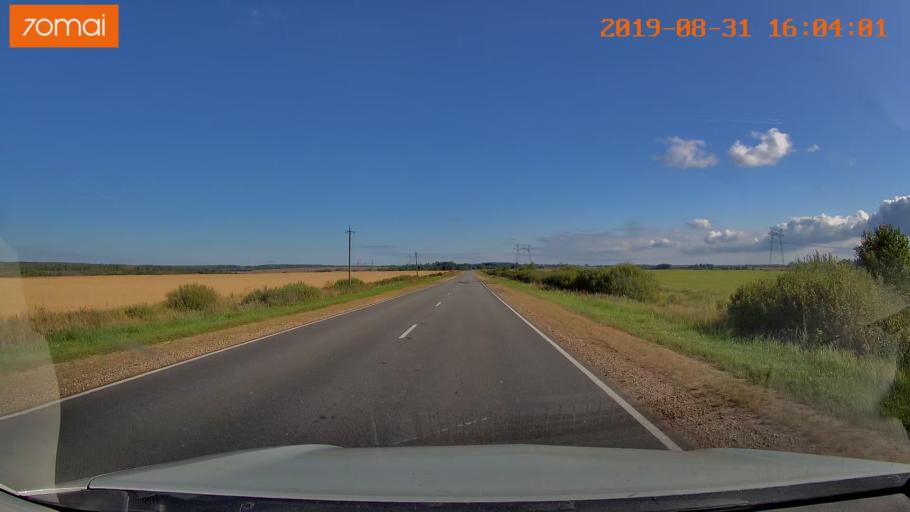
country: RU
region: Kaluga
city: Yukhnov
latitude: 54.6593
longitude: 35.3217
